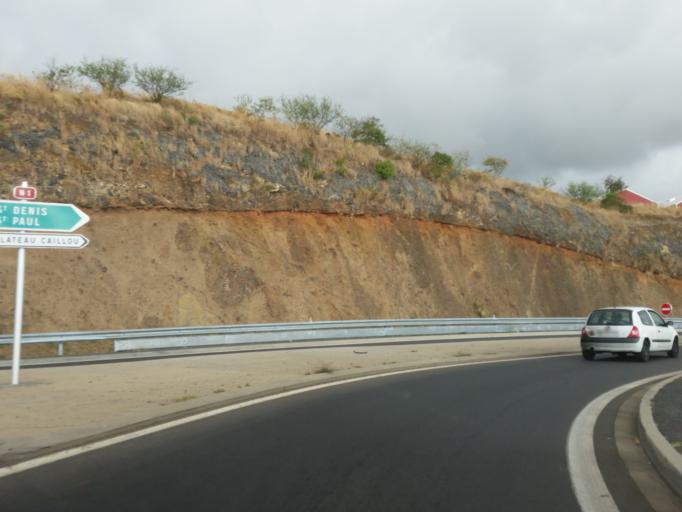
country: RE
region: Reunion
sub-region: Reunion
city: Saint-Paul
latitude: -21.0399
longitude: 55.2498
